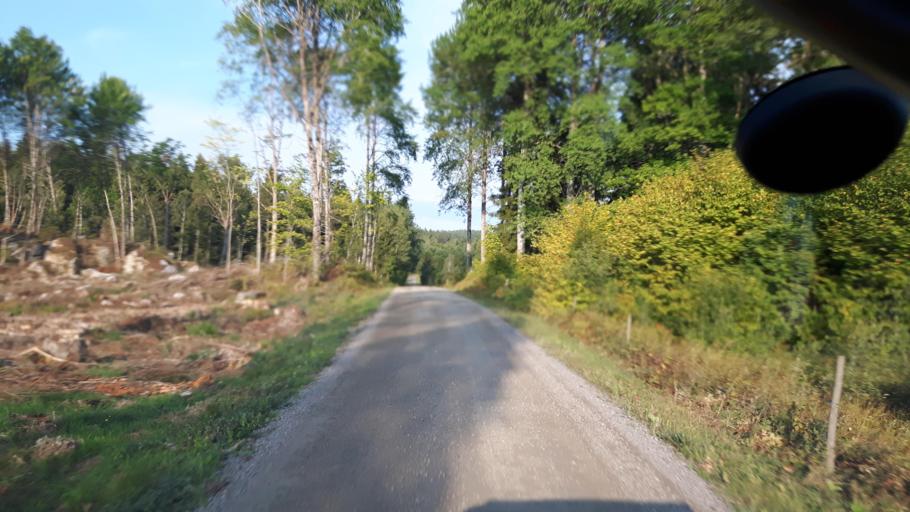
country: SE
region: OEstergoetland
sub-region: Kinda Kommun
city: Kisa
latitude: 58.0622
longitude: 15.6239
